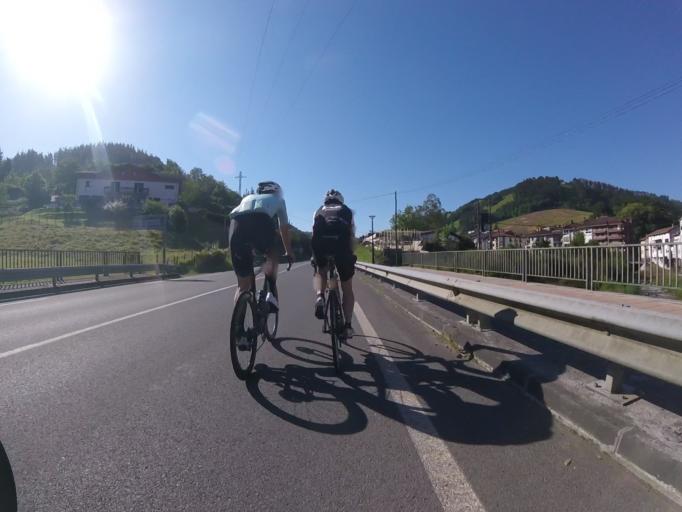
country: ES
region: Basque Country
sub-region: Provincia de Guipuzcoa
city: Azpeitia
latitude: 43.1585
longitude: -2.2441
